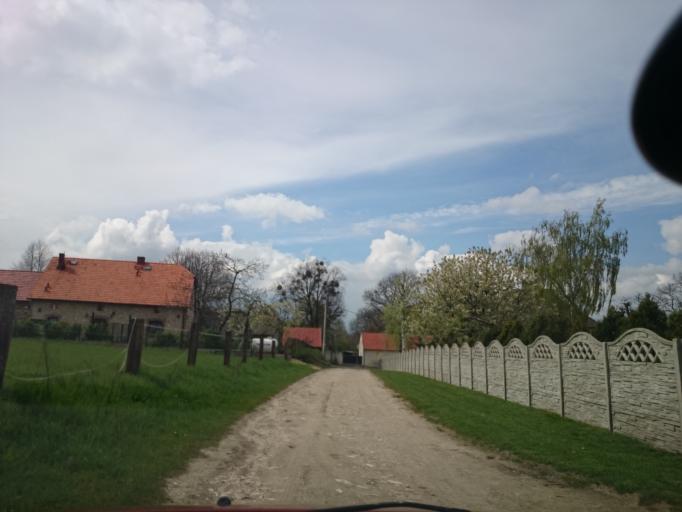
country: PL
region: Opole Voivodeship
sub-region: Powiat krapkowicki
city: Rozwadza
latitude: 50.4895
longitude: 18.1220
